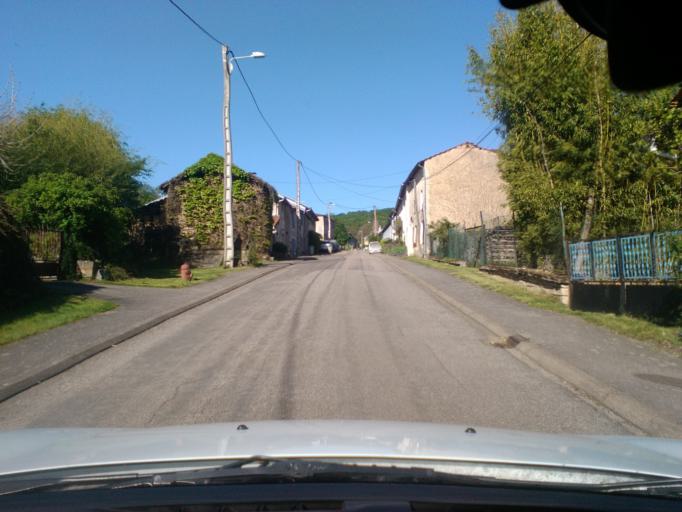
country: FR
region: Lorraine
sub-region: Departement des Vosges
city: Charmes
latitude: 48.3344
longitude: 6.2312
